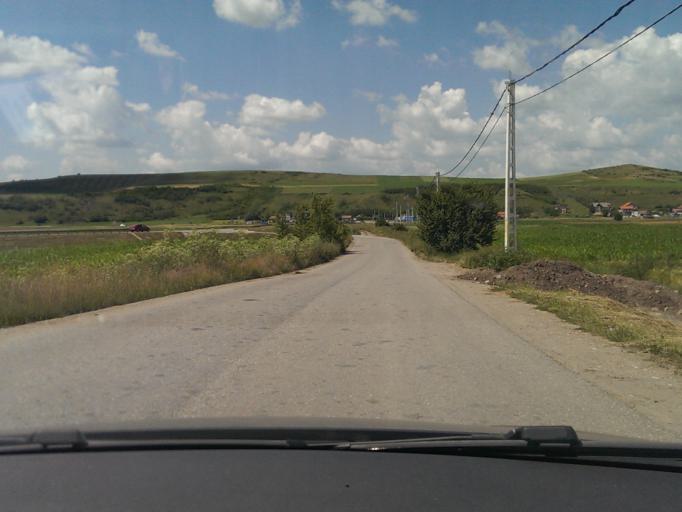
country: RO
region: Cluj
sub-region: Comuna Apahida
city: Sannicoara
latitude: 46.7938
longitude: 23.7191
